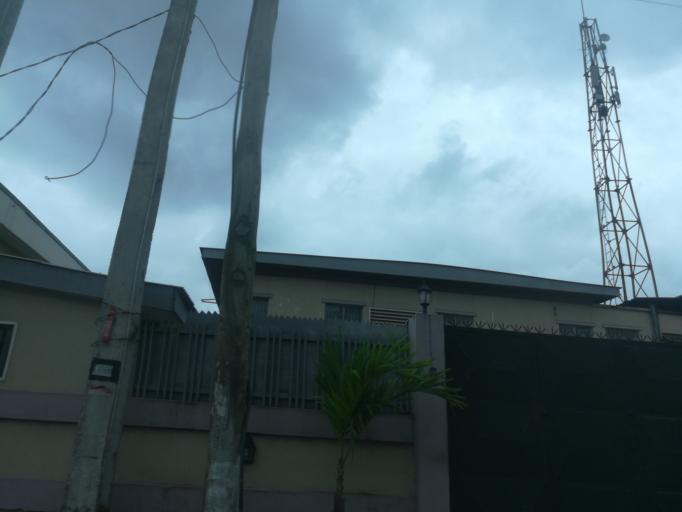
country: NG
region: Lagos
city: Ikeja
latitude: 6.6177
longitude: 3.3471
